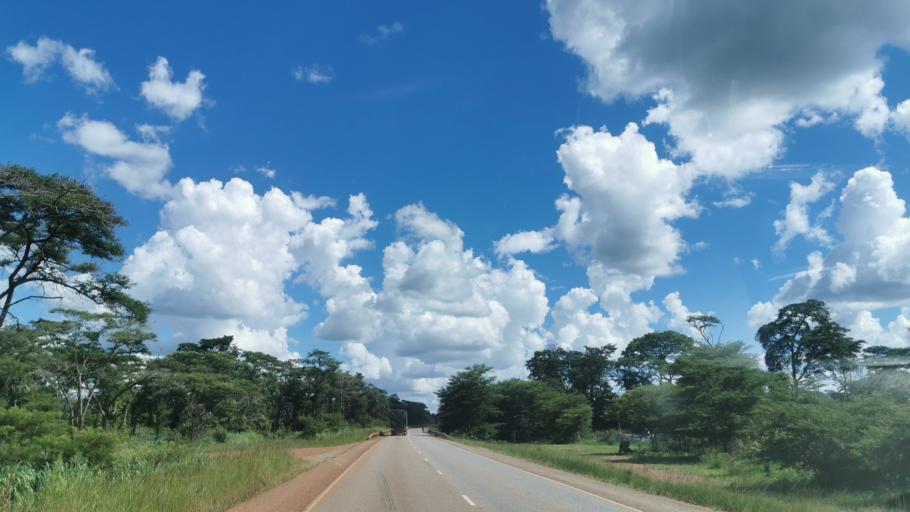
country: TZ
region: Geita
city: Uyovu
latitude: -3.0498
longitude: 31.2535
